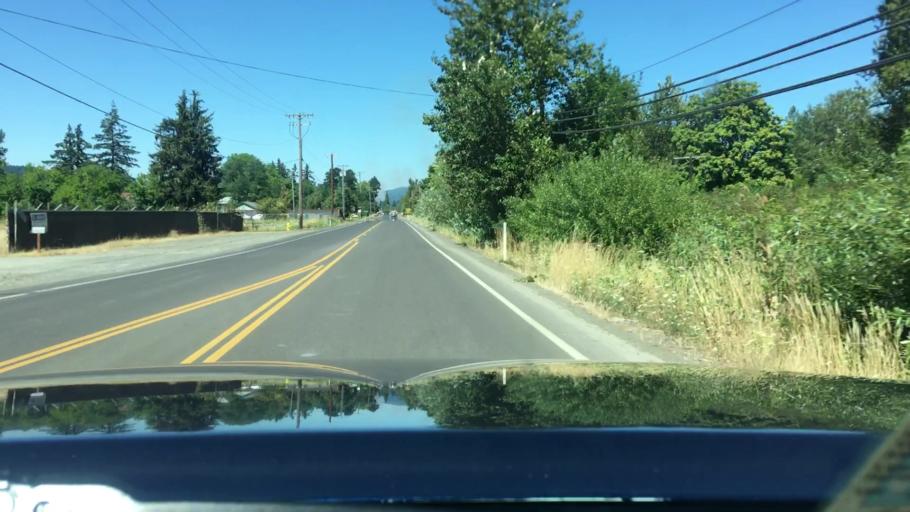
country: US
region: Oregon
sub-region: Lane County
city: Cottage Grove
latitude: 43.7808
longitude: -123.0710
